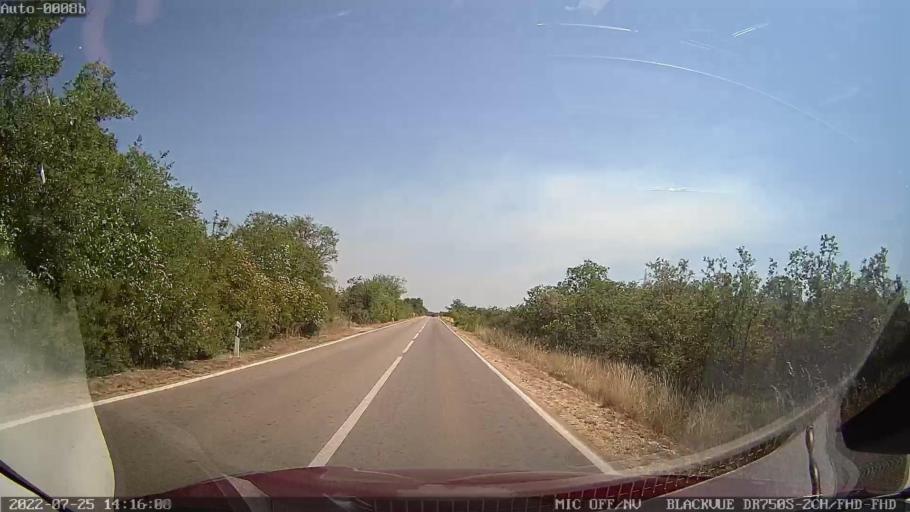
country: HR
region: Zadarska
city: Vrsi
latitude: 44.1937
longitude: 15.2572
